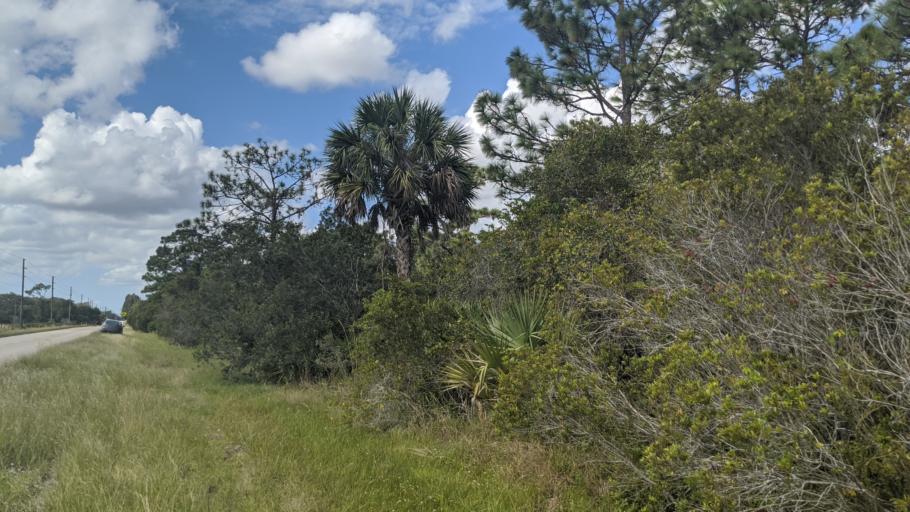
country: US
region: Florida
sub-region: Charlotte County
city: Cleveland
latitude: 26.9826
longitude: -81.8868
